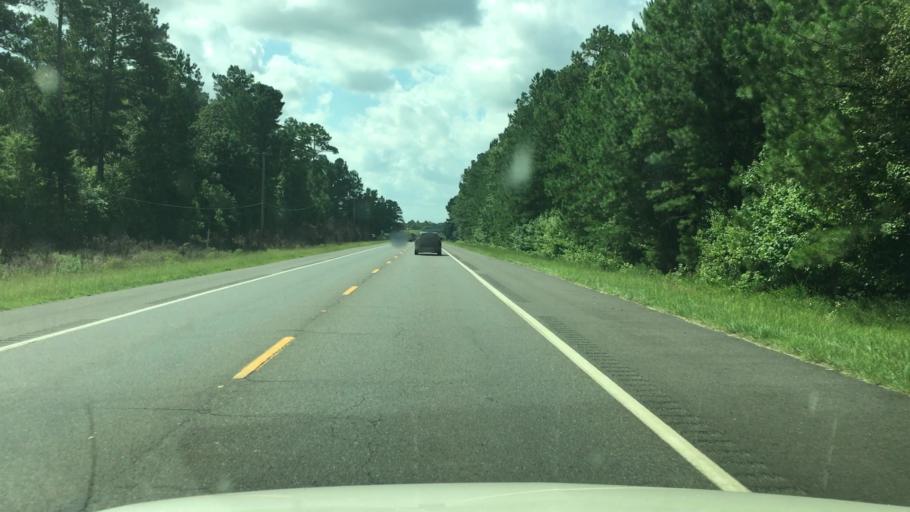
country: US
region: Arkansas
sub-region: Clark County
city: Arkadelphia
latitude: 34.1931
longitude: -93.0741
